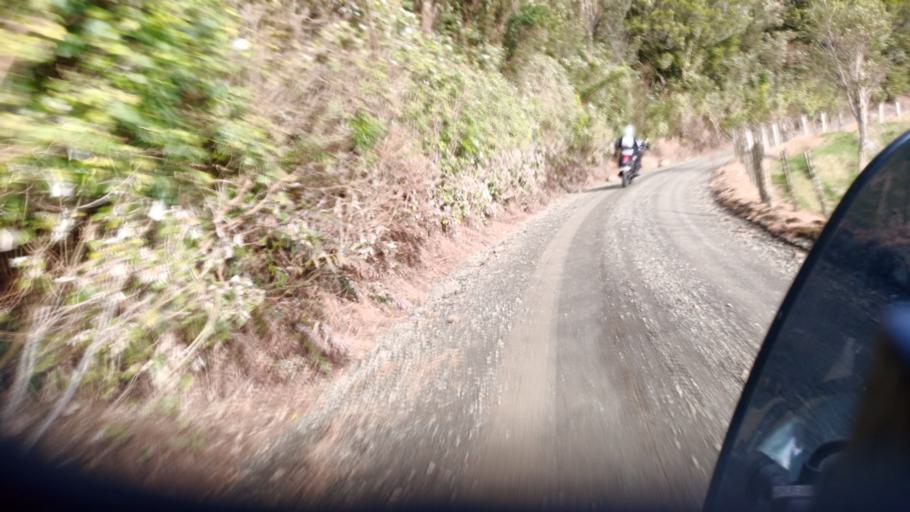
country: NZ
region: Gisborne
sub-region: Gisborne District
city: Gisborne
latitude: -38.4634
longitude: 177.5365
